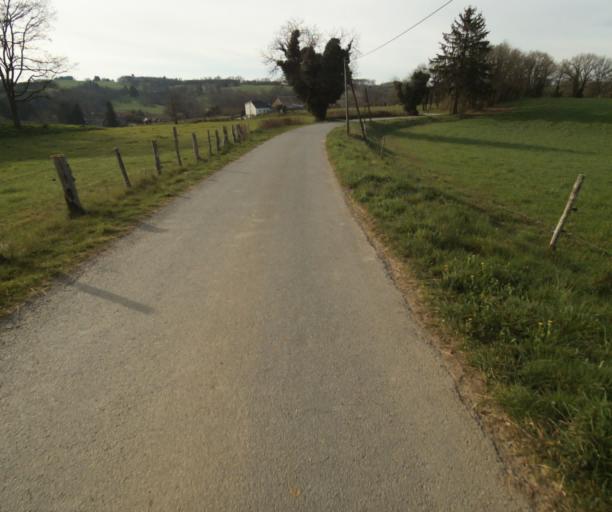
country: FR
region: Limousin
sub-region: Departement de la Correze
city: Chamboulive
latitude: 45.4486
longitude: 1.7505
